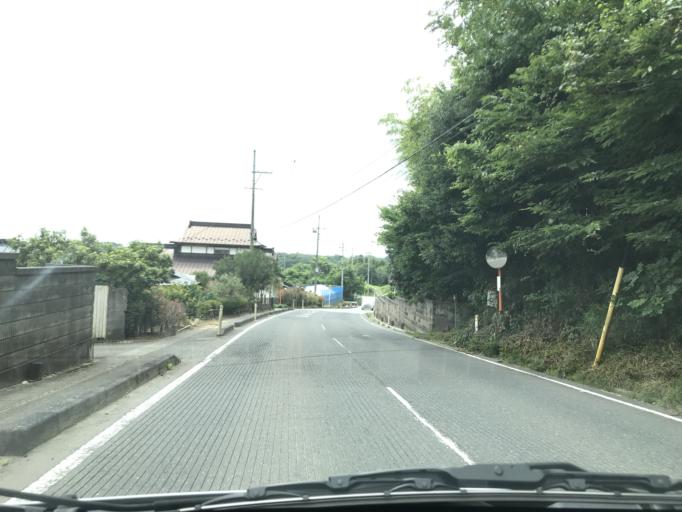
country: JP
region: Miyagi
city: Kogota
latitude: 38.7291
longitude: 141.0635
